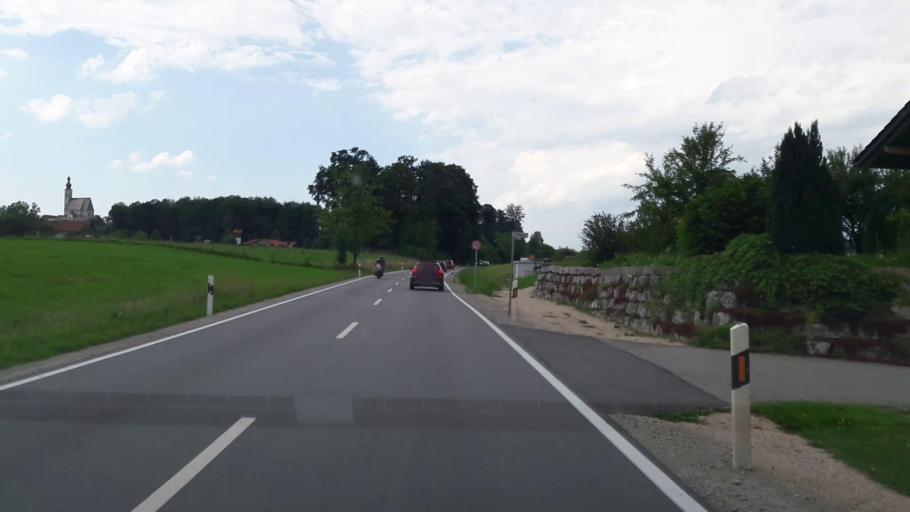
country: DE
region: Bavaria
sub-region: Upper Bavaria
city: Anger
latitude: 47.7963
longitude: 12.8674
